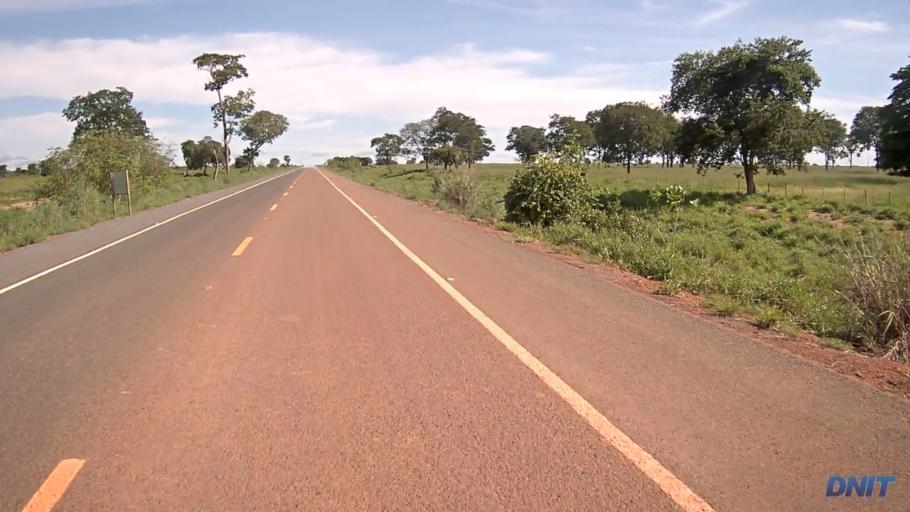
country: BR
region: Goias
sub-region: Sao Miguel Do Araguaia
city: Sao Miguel do Araguaia
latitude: -13.4980
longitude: -50.1069
